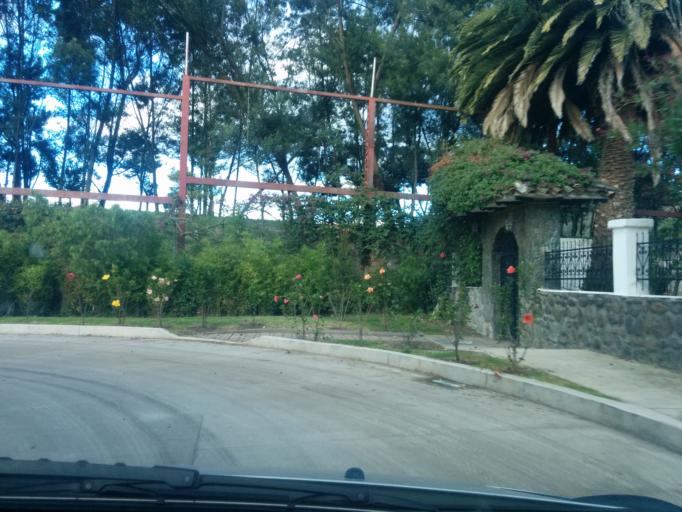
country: EC
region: Azuay
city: Llacao
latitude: -2.8769
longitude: -78.9447
